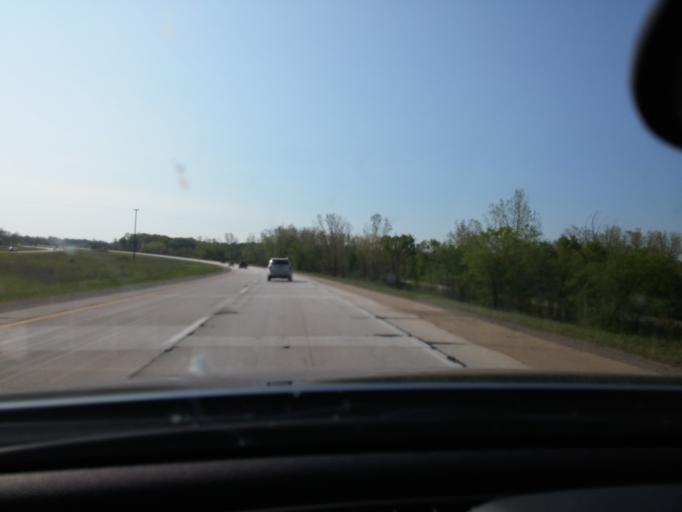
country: US
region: Michigan
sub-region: Lapeer County
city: Imlay City
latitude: 43.0008
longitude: -83.1470
